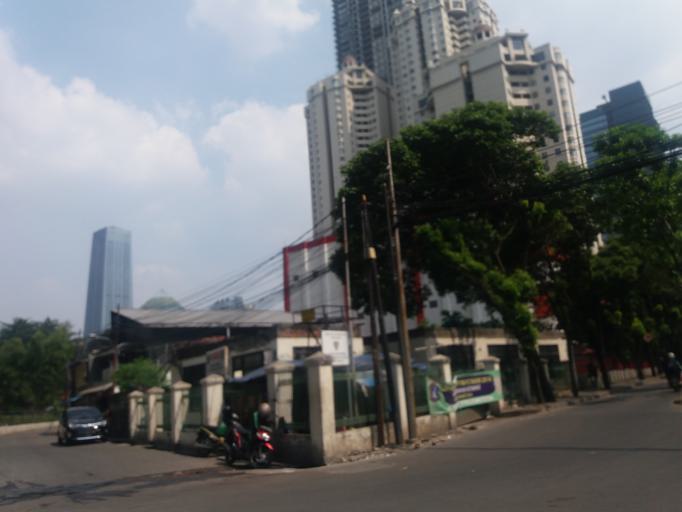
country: ID
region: Jakarta Raya
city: Jakarta
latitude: -6.2187
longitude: 106.8169
